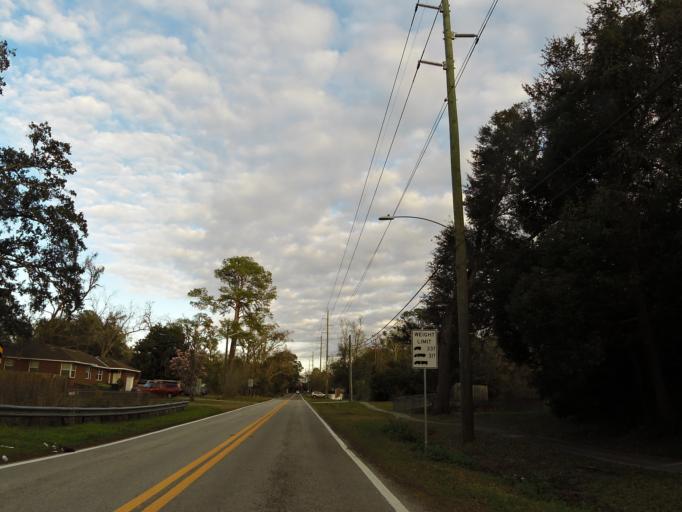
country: US
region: Florida
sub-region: Duval County
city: Jacksonville
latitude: 30.3031
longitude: -81.7255
